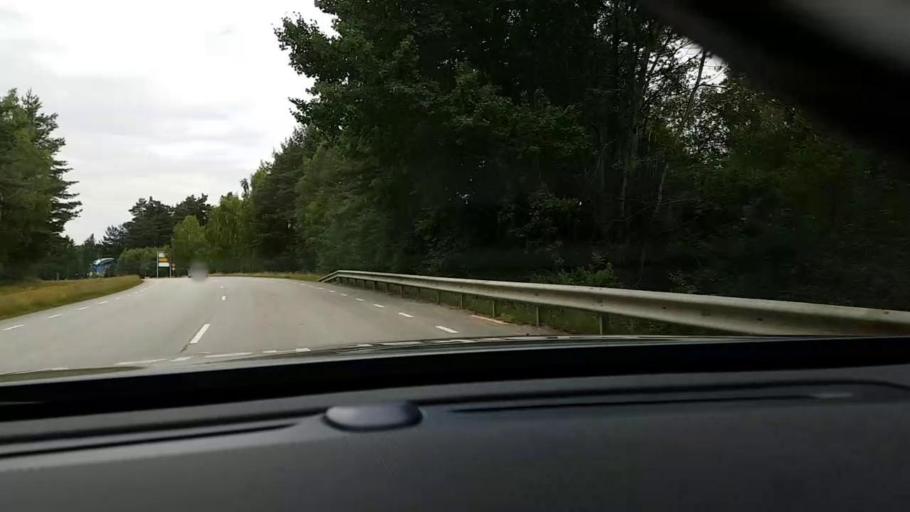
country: SE
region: Skane
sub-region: Hassleholms Kommun
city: Hassleholm
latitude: 56.1648
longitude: 13.8052
